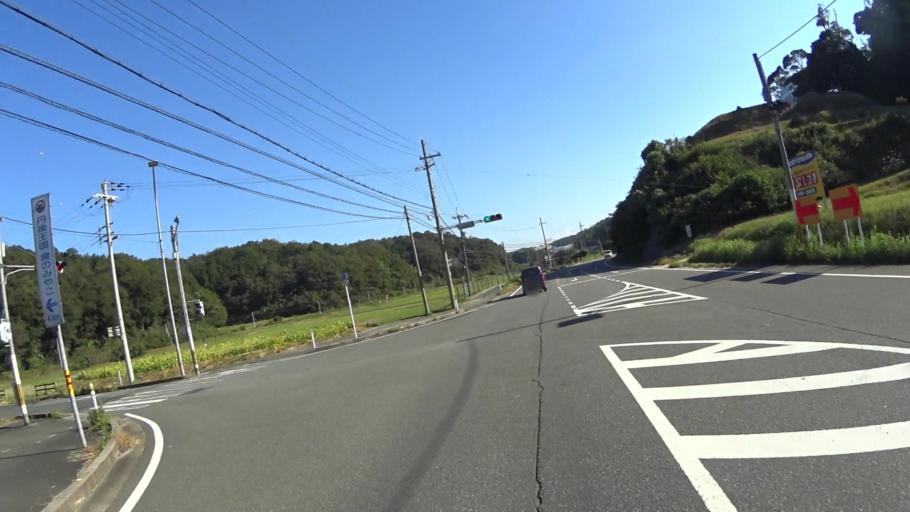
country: JP
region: Kyoto
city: Miyazu
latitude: 35.6445
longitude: 135.0504
